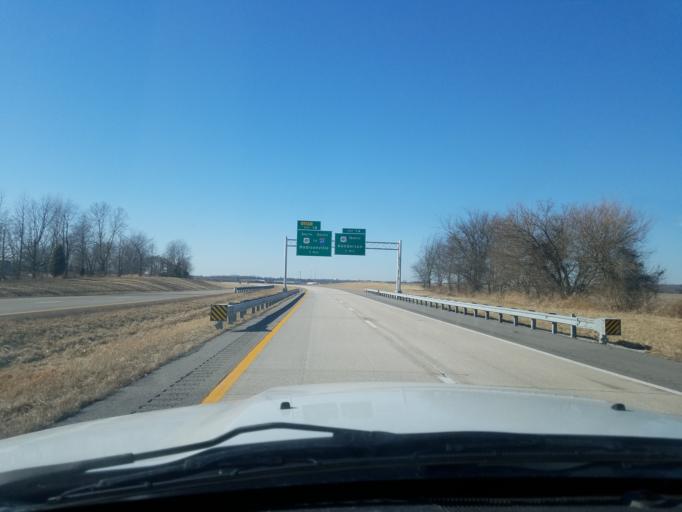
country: US
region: Kentucky
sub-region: Henderson County
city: Henderson
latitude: 37.8090
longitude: -87.5402
